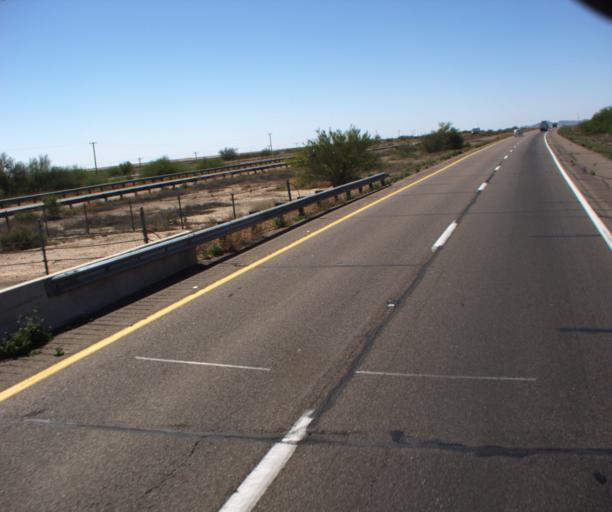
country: US
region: Arizona
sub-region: Maricopa County
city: Gila Bend
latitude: 32.9283
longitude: -112.8358
